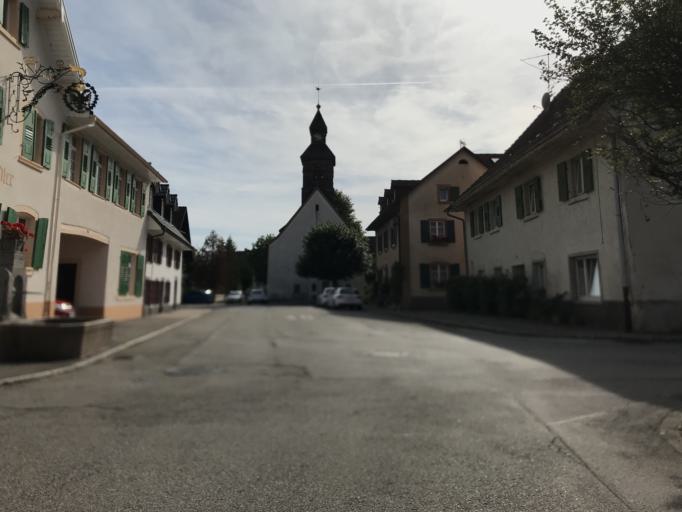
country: DE
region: Baden-Wuerttemberg
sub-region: Freiburg Region
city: Hausen
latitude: 47.6812
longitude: 7.8417
